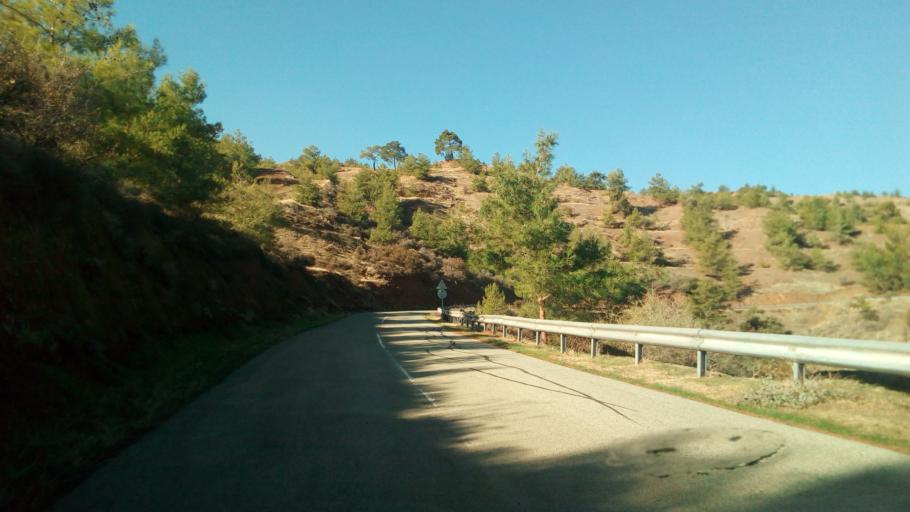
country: CY
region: Lefkosia
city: Lefka
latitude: 35.0889
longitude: 32.7969
